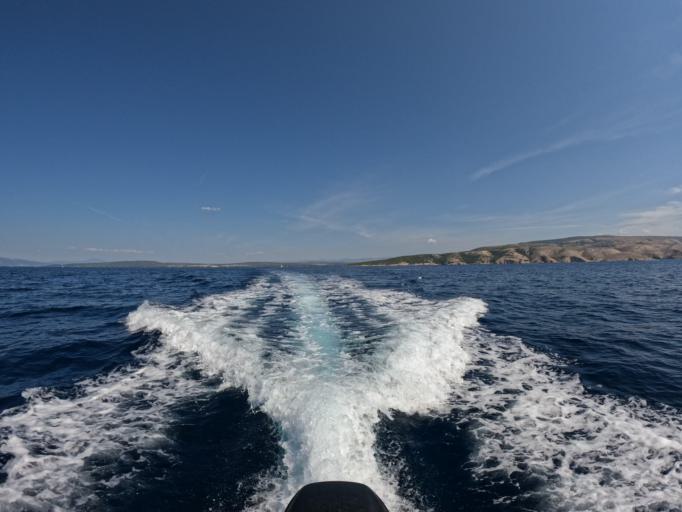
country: HR
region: Primorsko-Goranska
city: Punat
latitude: 44.9531
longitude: 14.6119
